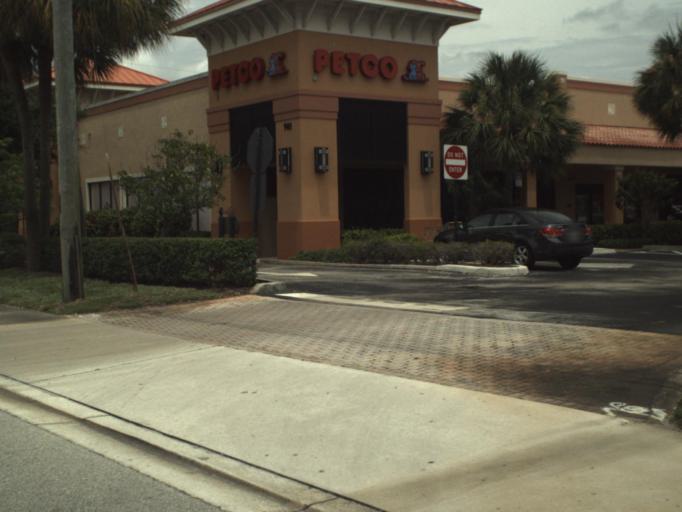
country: US
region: Florida
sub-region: Palm Beach County
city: Jupiter
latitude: 26.9341
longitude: -80.1111
